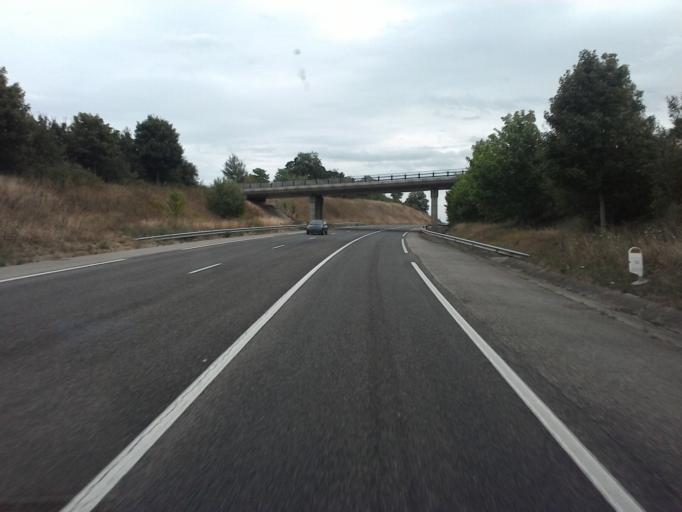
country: FR
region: Lorraine
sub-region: Departement de Meurthe-et-Moselle
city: Bainville-sur-Madon
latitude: 48.5809
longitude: 6.0255
